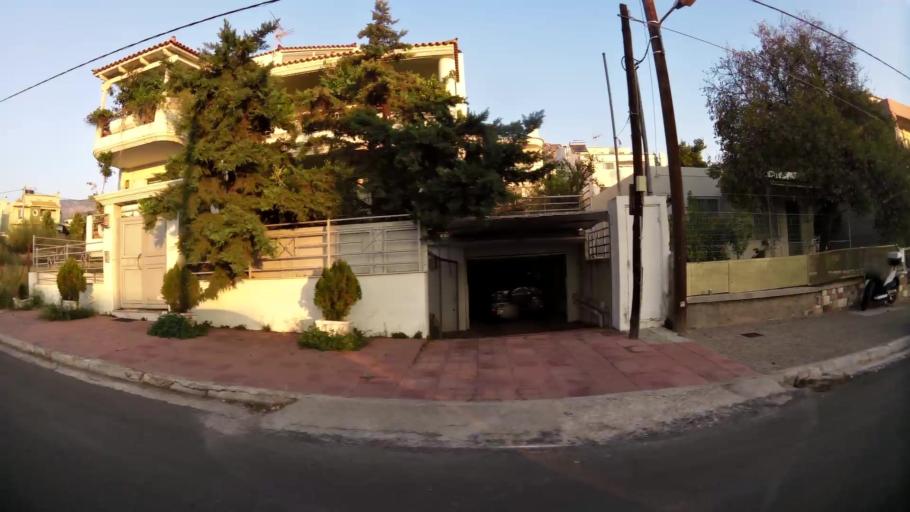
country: GR
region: Attica
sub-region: Nomarchia Athinas
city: Glyfada
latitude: 37.8809
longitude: 23.7710
